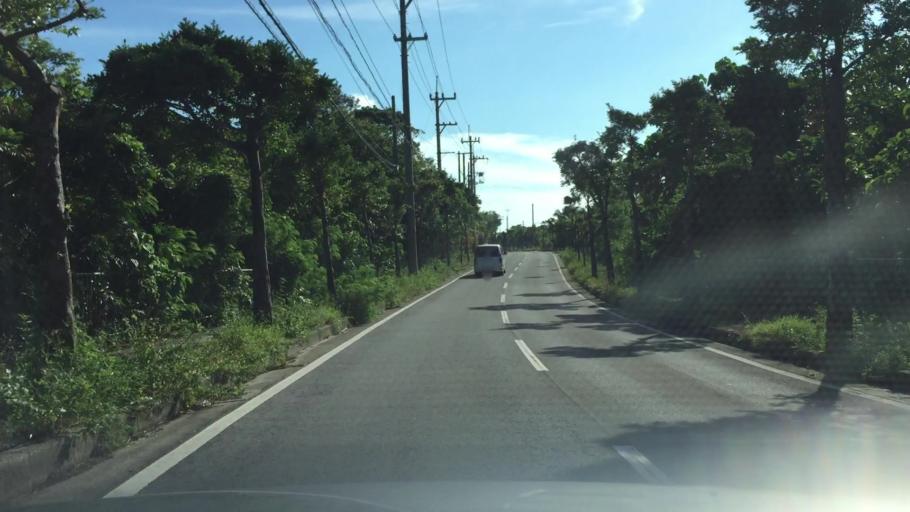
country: JP
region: Okinawa
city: Ishigaki
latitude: 24.4468
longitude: 124.1536
